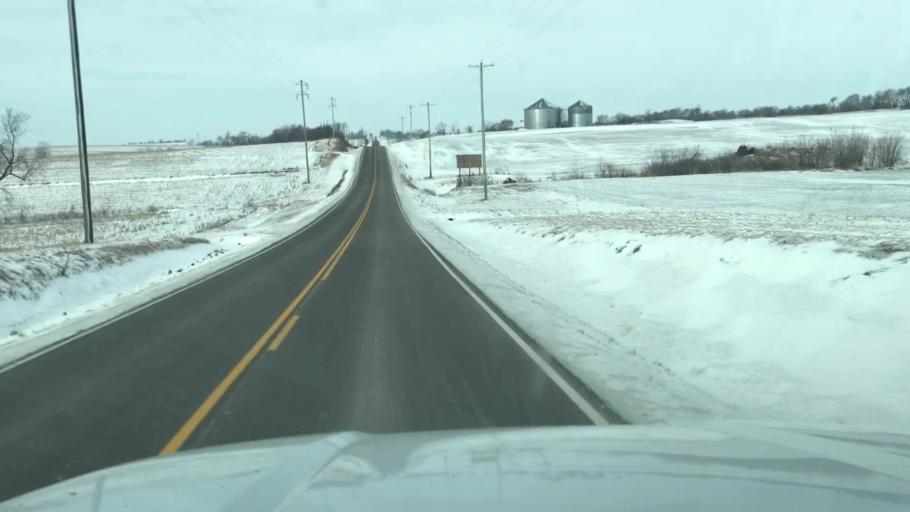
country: US
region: Missouri
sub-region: Holt County
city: Mound City
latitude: 40.1301
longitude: -95.0963
